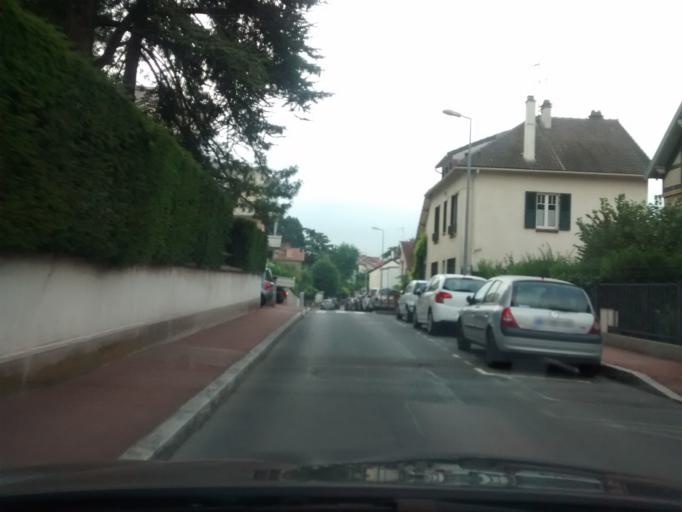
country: FR
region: Ile-de-France
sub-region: Departement des Yvelines
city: Viroflay
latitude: 48.8073
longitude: 2.1710
